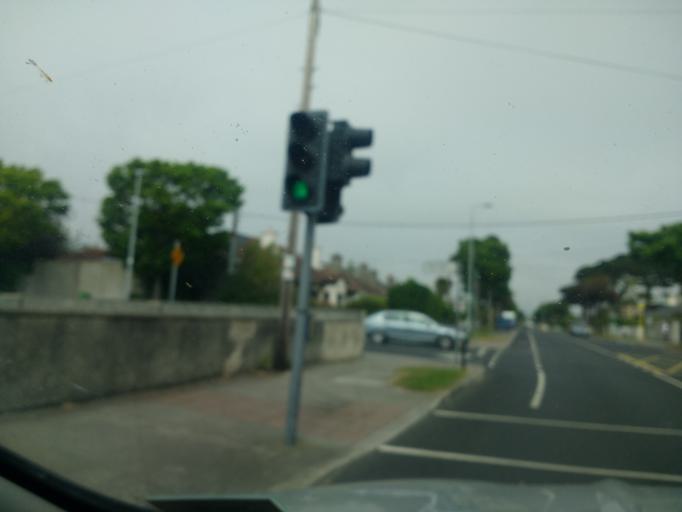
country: IE
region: Leinster
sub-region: Fingal County
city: Baldoyle
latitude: 53.3926
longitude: -6.1250
